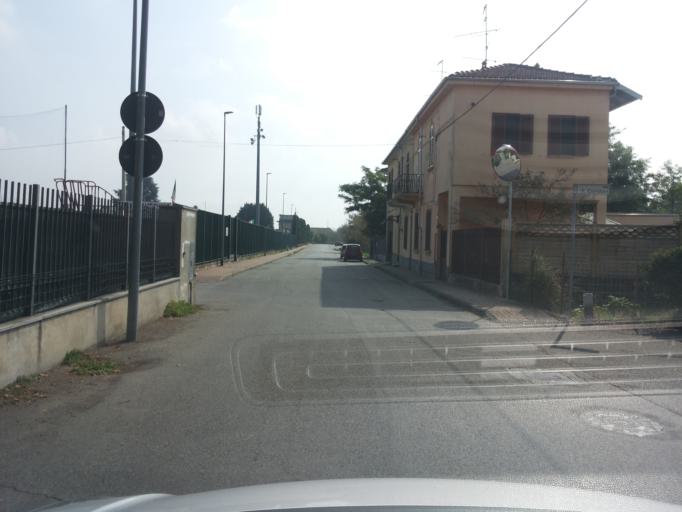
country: IT
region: Piedmont
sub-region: Provincia di Vercelli
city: Vercelli
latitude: 45.3044
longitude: 8.4471
